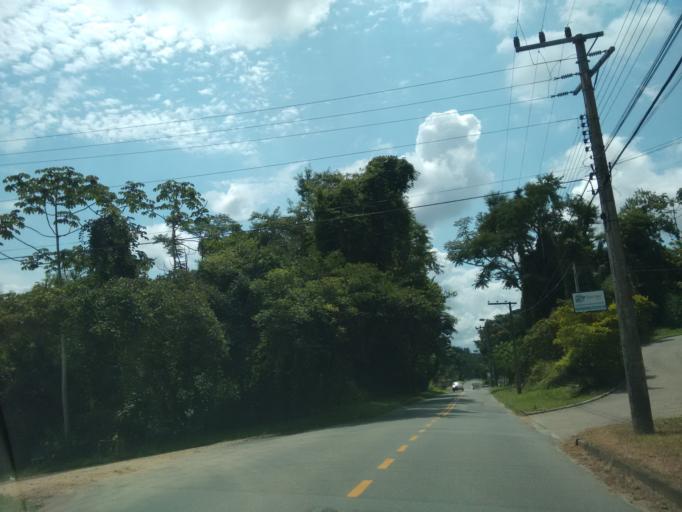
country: BR
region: Santa Catarina
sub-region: Blumenau
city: Blumenau
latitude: -26.8649
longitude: -49.1400
